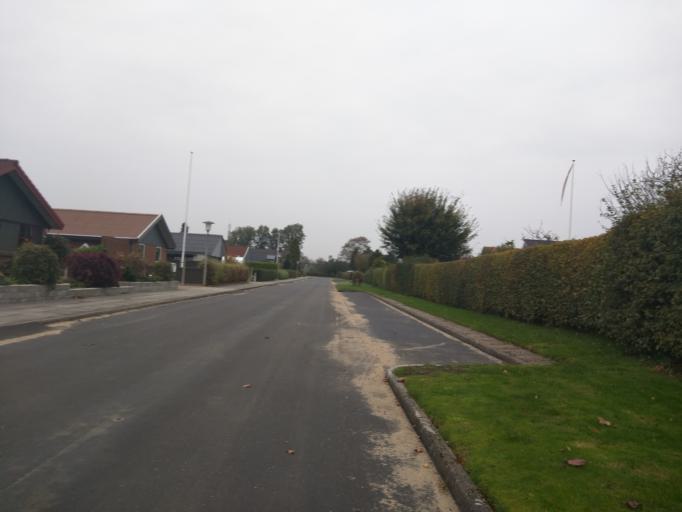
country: DK
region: Central Jutland
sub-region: Viborg Kommune
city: Viborg
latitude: 56.4569
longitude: 9.3866
